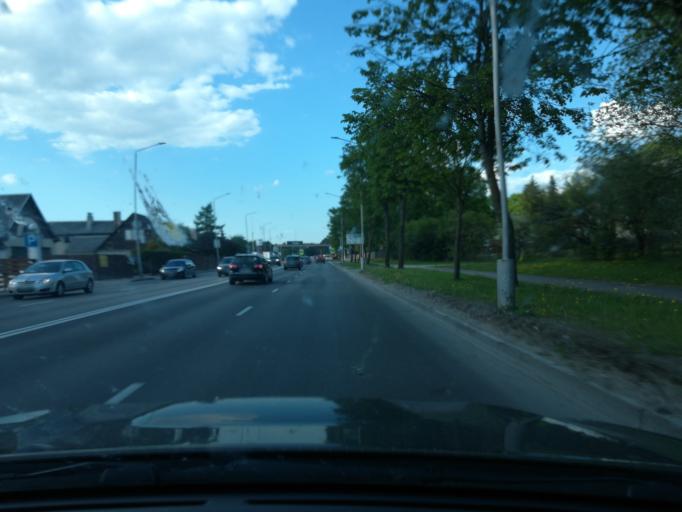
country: LT
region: Kauno apskritis
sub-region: Kaunas
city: Eiguliai
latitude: 54.9327
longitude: 23.9177
